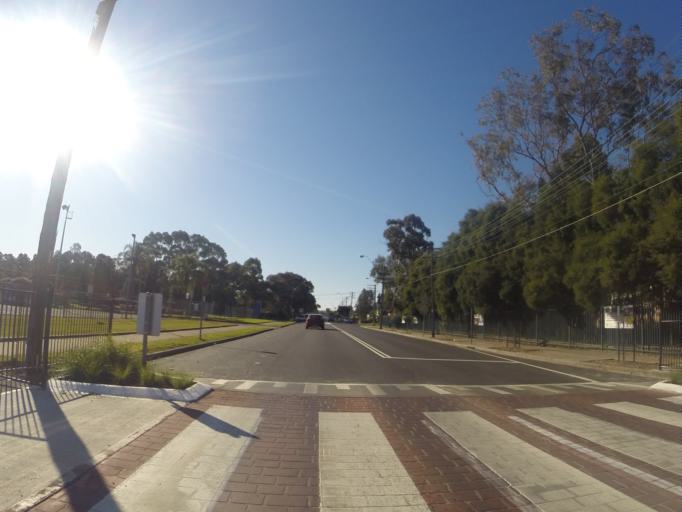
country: AU
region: New South Wales
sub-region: Auburn
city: Auburn
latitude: -33.8606
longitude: 151.0190
